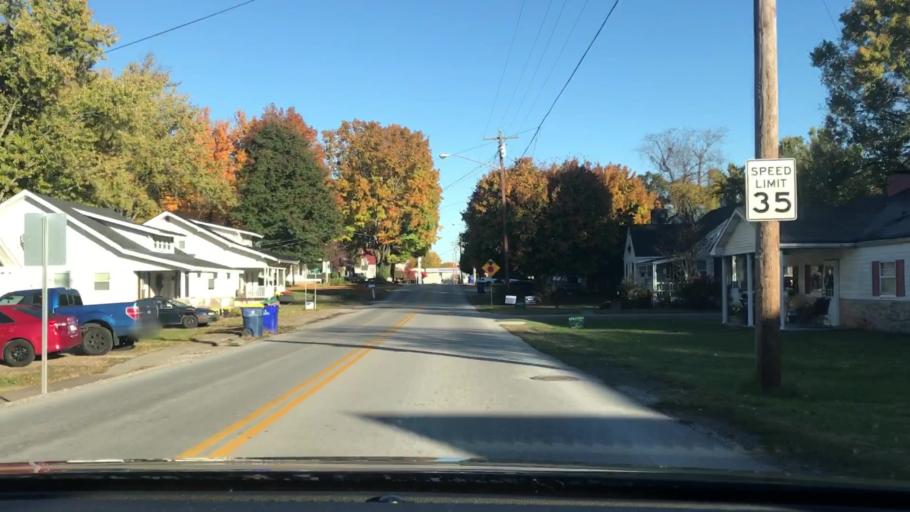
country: US
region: Kentucky
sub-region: Logan County
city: Auburn
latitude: 36.8605
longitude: -86.7117
